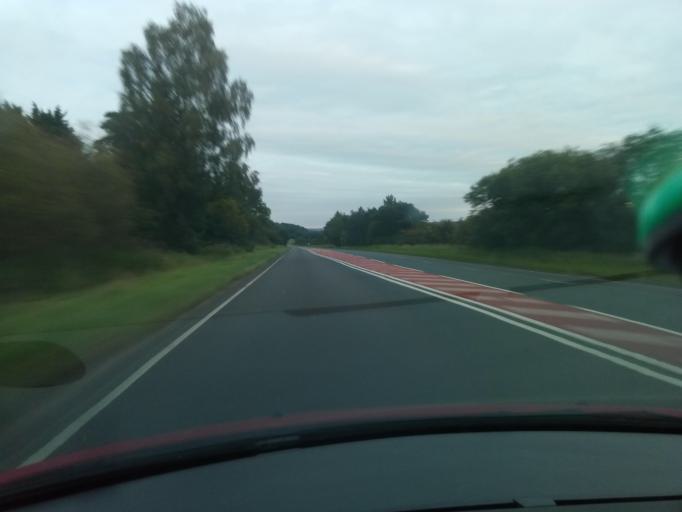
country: GB
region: England
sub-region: Northumberland
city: Haltwhistle
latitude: 54.9698
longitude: -2.4183
